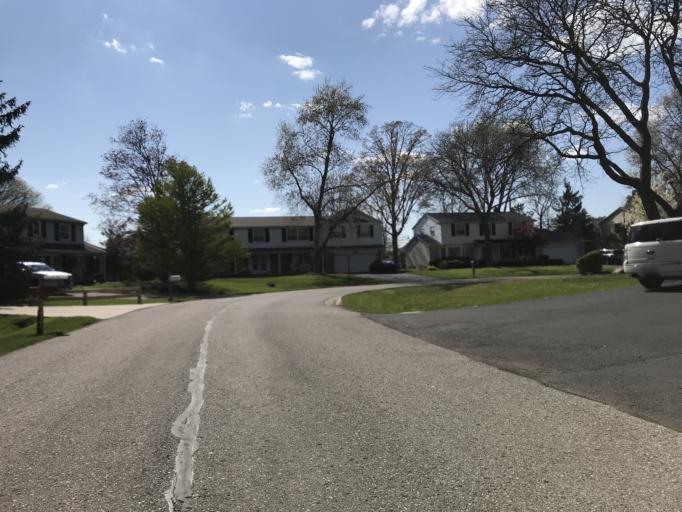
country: US
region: Michigan
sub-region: Oakland County
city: Farmington Hills
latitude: 42.4785
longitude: -83.3321
